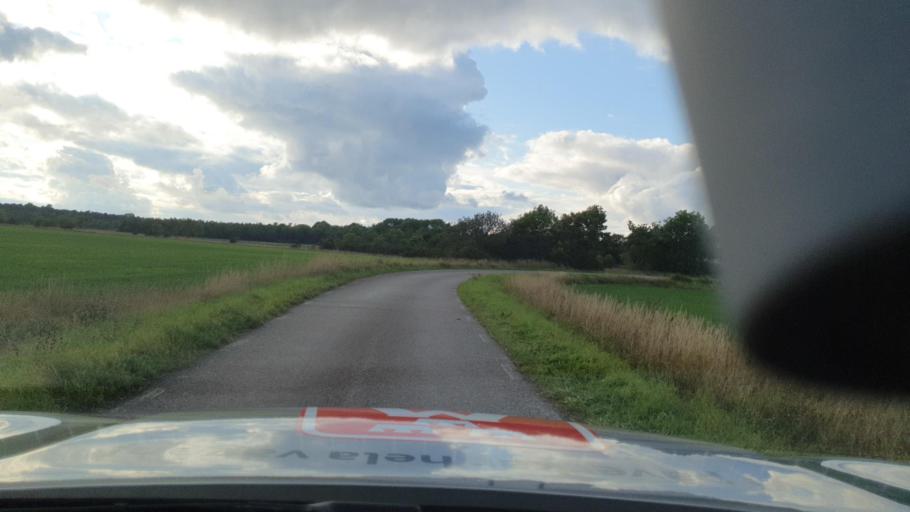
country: SE
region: Gotland
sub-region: Gotland
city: Hemse
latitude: 57.2008
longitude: 18.2514
